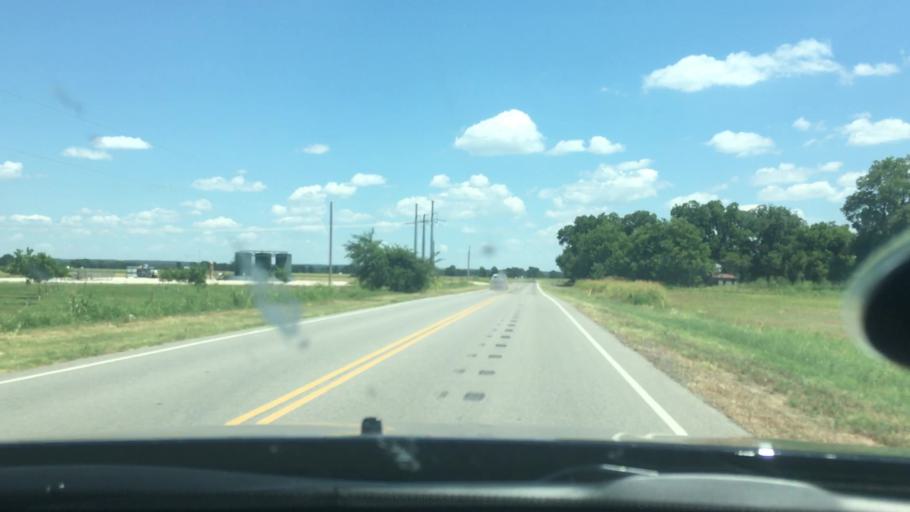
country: US
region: Oklahoma
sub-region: Carter County
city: Dickson
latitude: 34.2432
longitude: -96.9739
